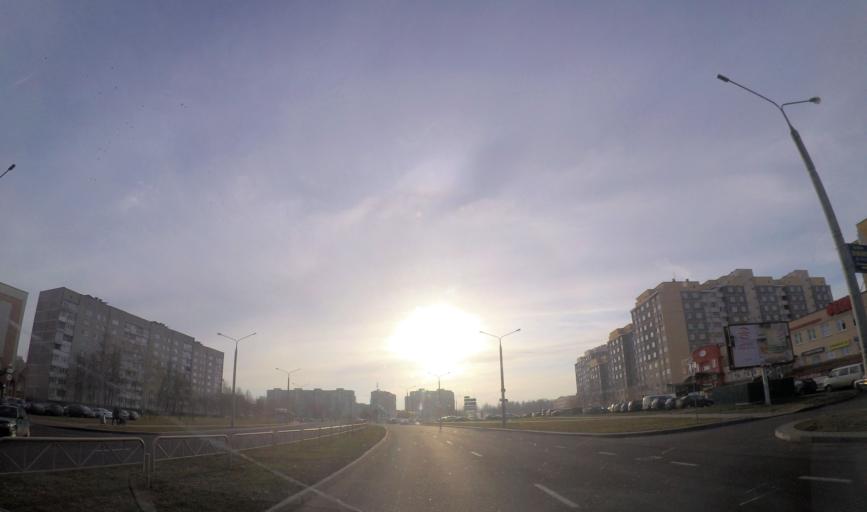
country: BY
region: Grodnenskaya
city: Hrodna
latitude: 53.6595
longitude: 23.7820
